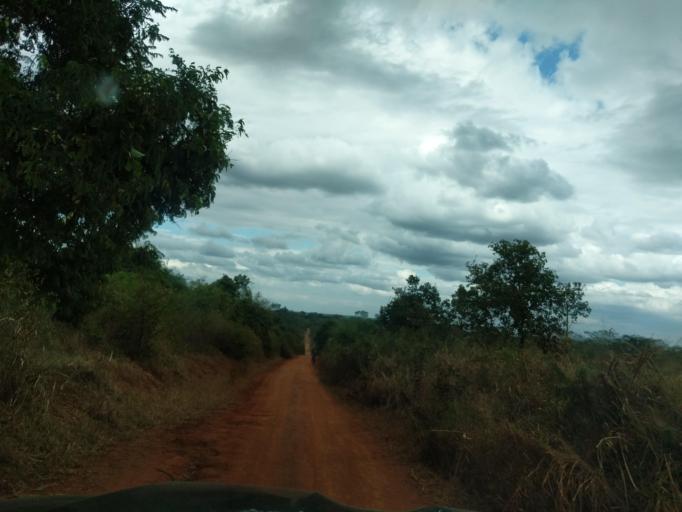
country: TZ
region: Pwani
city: Mvomero
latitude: -5.9328
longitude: 38.4200
